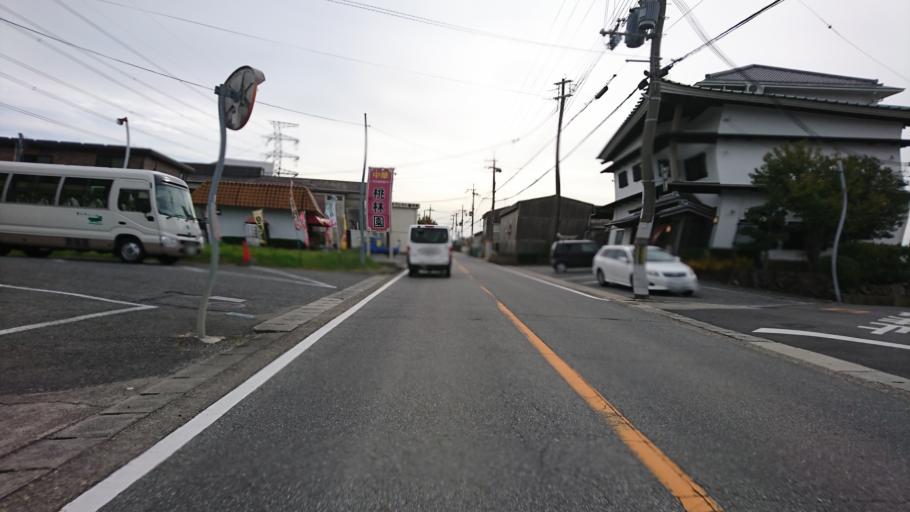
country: JP
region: Hyogo
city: Ono
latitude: 34.8003
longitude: 134.9248
